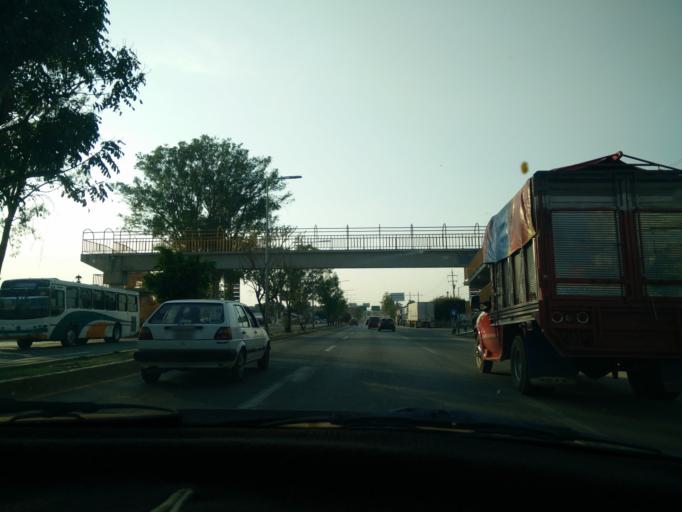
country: MX
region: Oaxaca
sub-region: Santa Maria Atzompa
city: Fraccionamiento Riberas de San Jeronimo
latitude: 17.1283
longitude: -96.7690
